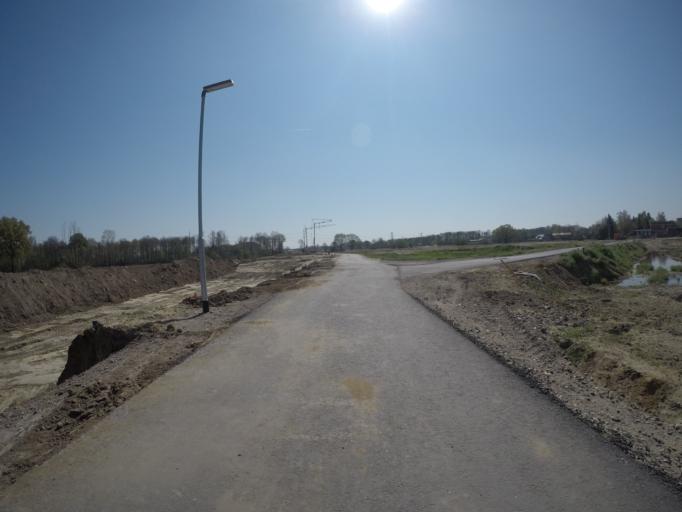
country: DE
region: North Rhine-Westphalia
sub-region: Regierungsbezirk Munster
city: Isselburg
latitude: 51.8502
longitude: 6.4352
